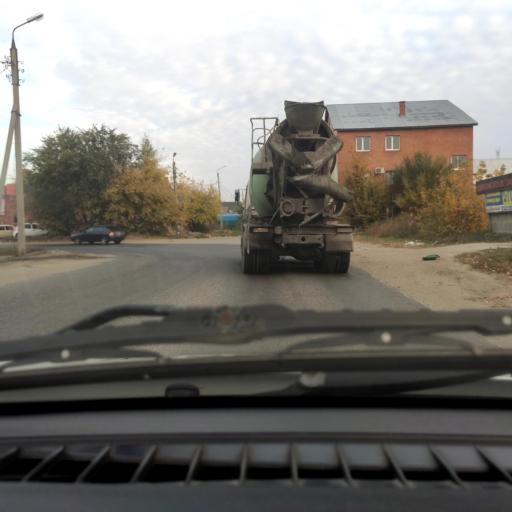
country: RU
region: Samara
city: Tol'yatti
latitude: 53.5390
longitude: 49.4252
